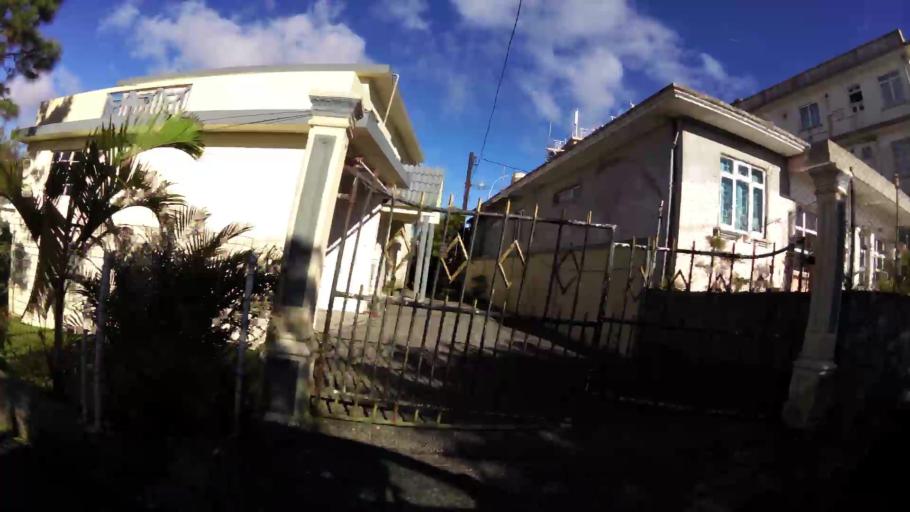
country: MU
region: Plaines Wilhems
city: Curepipe
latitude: -20.3207
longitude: 57.5361
